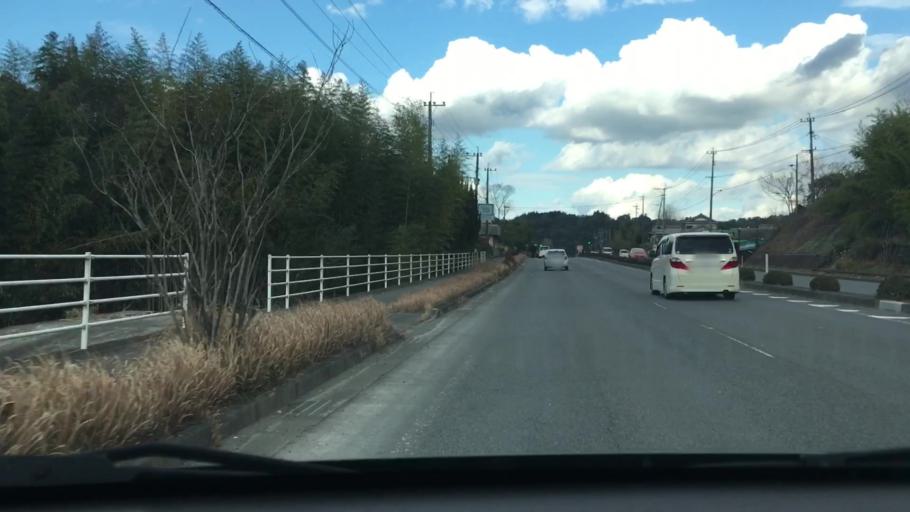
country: JP
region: Oita
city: Oita
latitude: 33.1275
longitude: 131.6566
